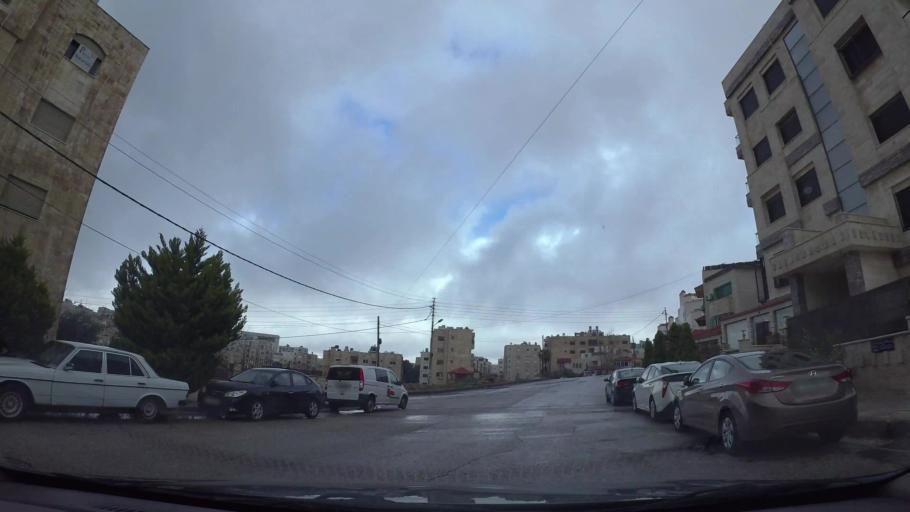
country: JO
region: Amman
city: Wadi as Sir
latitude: 31.9427
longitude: 35.8549
